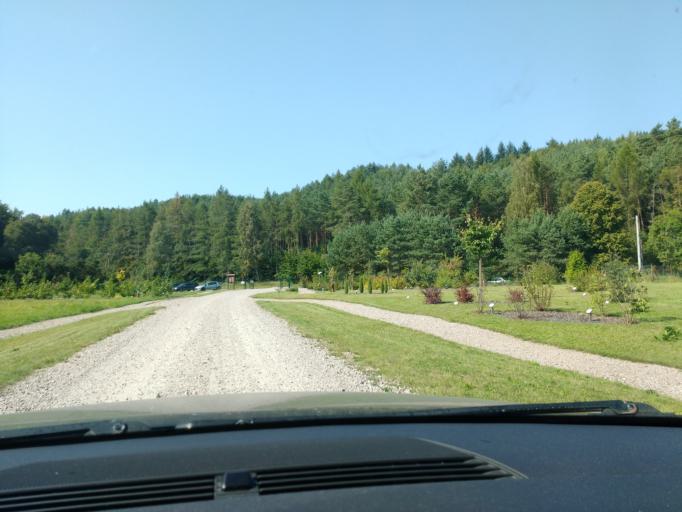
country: PL
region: Pomeranian Voivodeship
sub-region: Powiat wejherowski
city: Bojano
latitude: 54.5195
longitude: 18.4163
